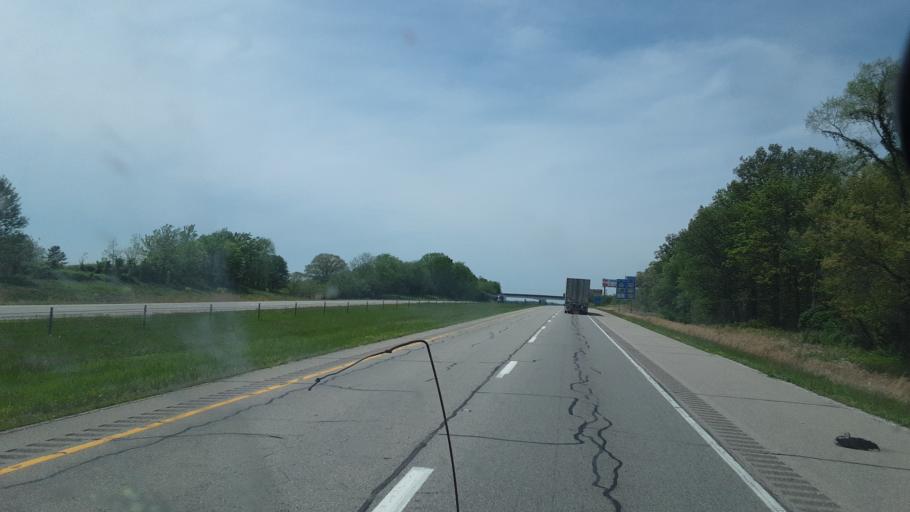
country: US
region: Indiana
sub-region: Gibson County
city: Haubstadt
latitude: 38.1662
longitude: -87.5250
